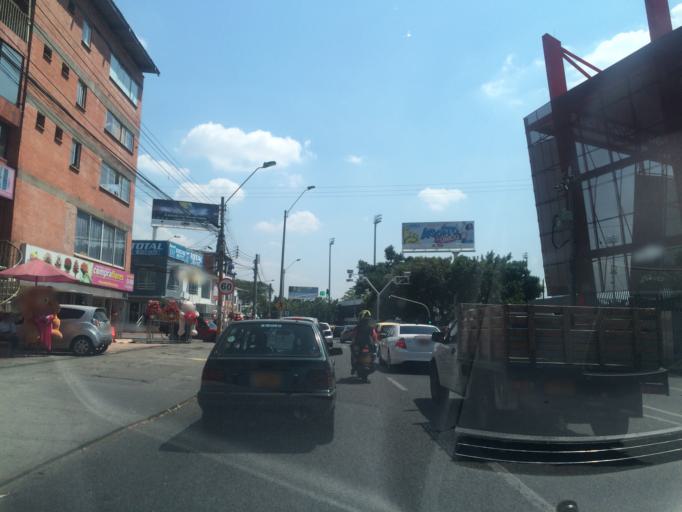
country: CO
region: Valle del Cauca
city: Cali
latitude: 3.4220
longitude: -76.5384
